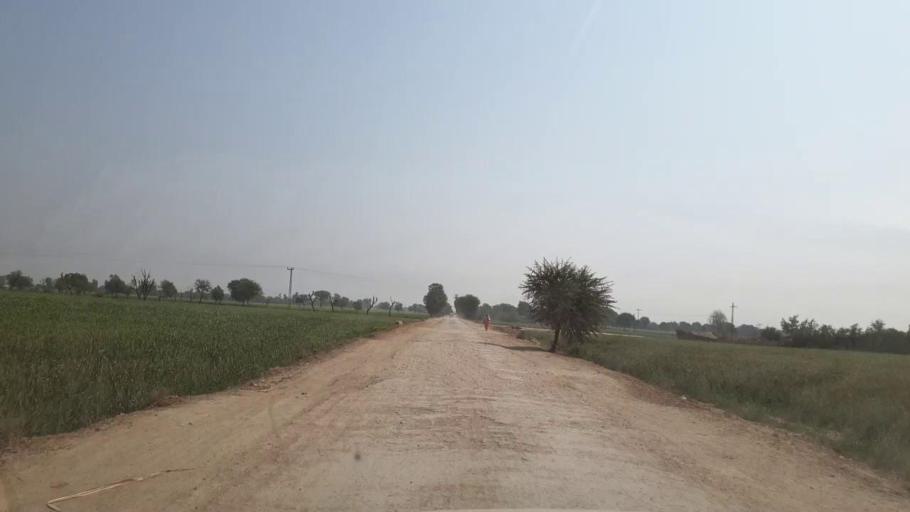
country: PK
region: Sindh
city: Mirpur Khas
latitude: 25.6534
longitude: 69.1451
